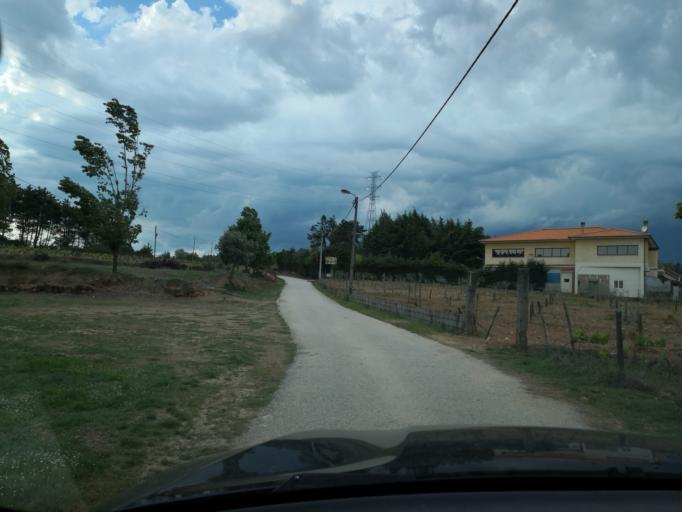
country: PT
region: Vila Real
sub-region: Sabrosa
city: Vilela
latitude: 41.2205
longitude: -7.6688
